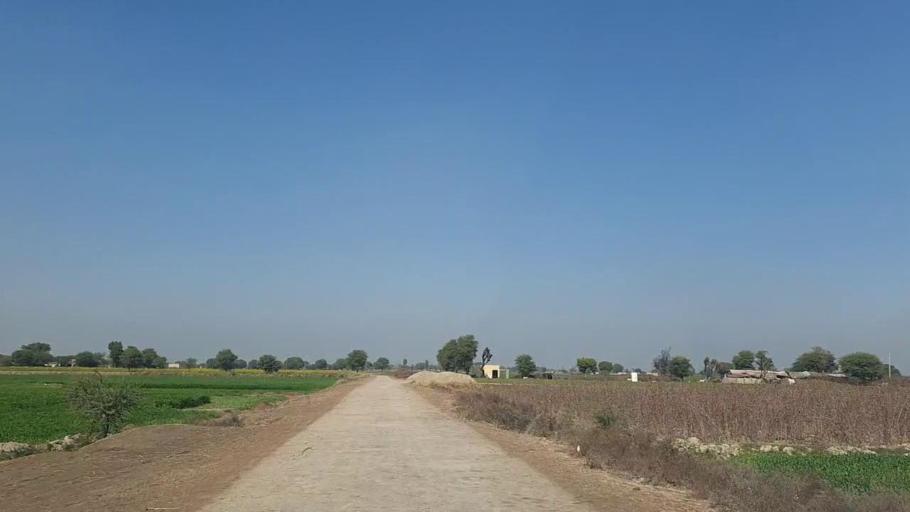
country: PK
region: Sindh
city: Shahpur Chakar
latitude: 26.1990
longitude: 68.5662
